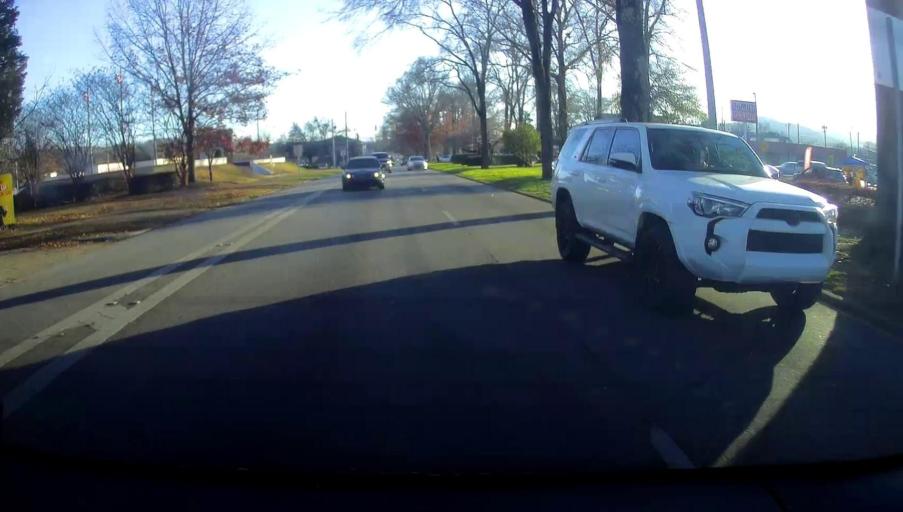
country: US
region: Alabama
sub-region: Calhoun County
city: Anniston
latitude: 33.6674
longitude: -85.8266
